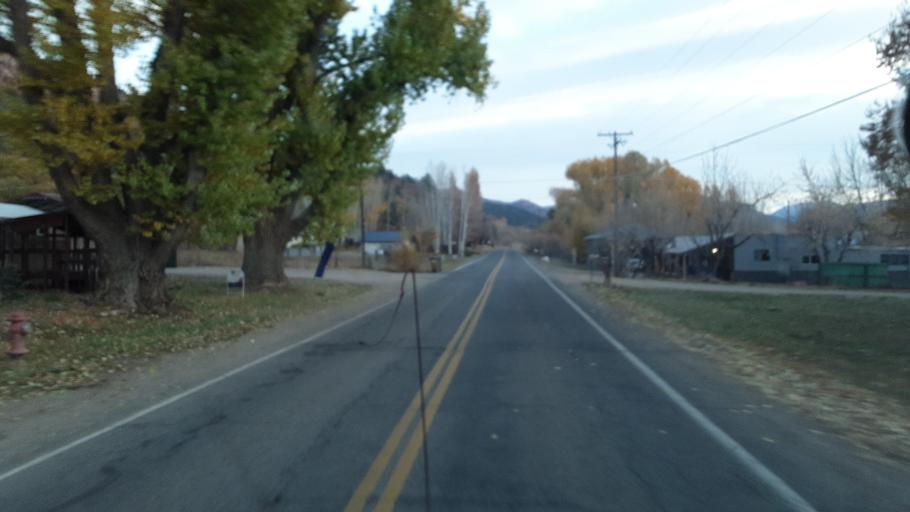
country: US
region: Colorado
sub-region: La Plata County
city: Durango
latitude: 37.3349
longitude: -107.8551
